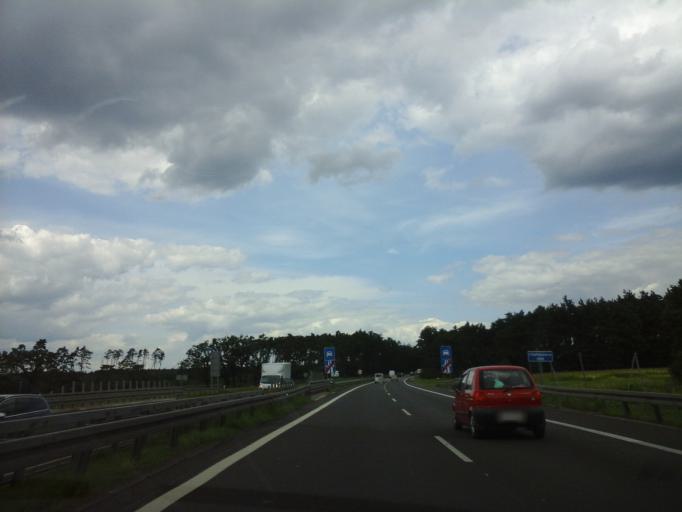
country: PL
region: West Pomeranian Voivodeship
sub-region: Powiat gryfinski
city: Stare Czarnowo
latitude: 53.4035
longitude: 14.7230
